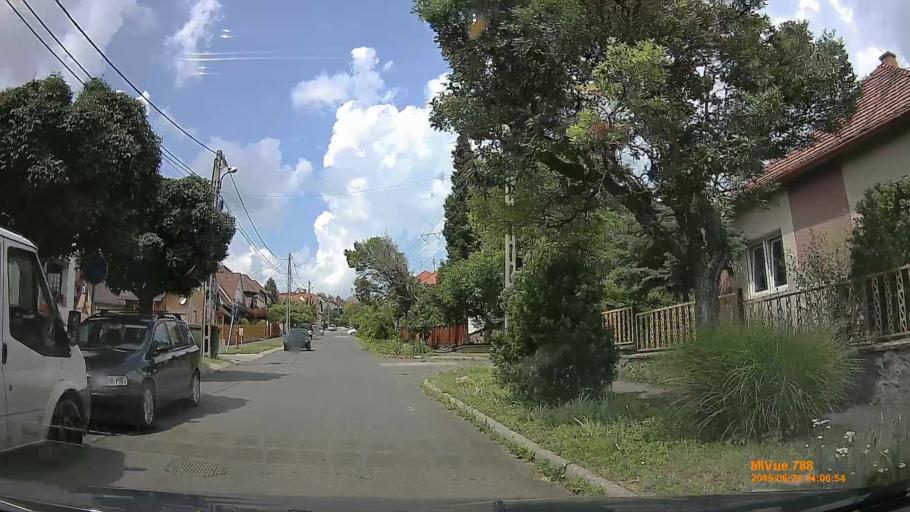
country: HU
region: Baranya
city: Pellerd
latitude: 46.0674
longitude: 18.1698
